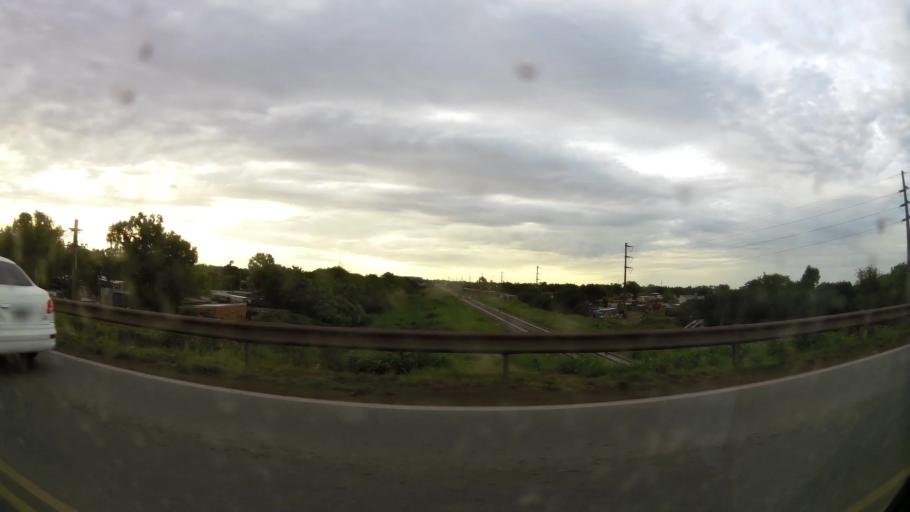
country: AR
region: Buenos Aires
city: San Nicolas de los Arroyos
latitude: -33.3658
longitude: -60.1954
